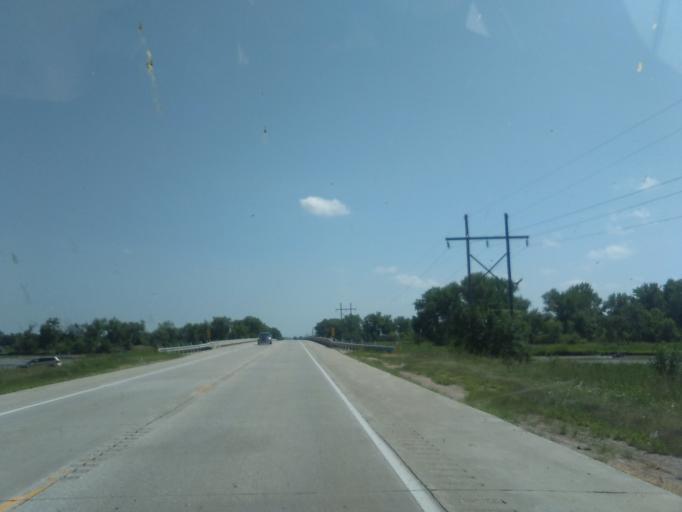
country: US
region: Nebraska
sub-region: Phelps County
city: Holdrege
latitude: 40.6840
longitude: -99.3804
